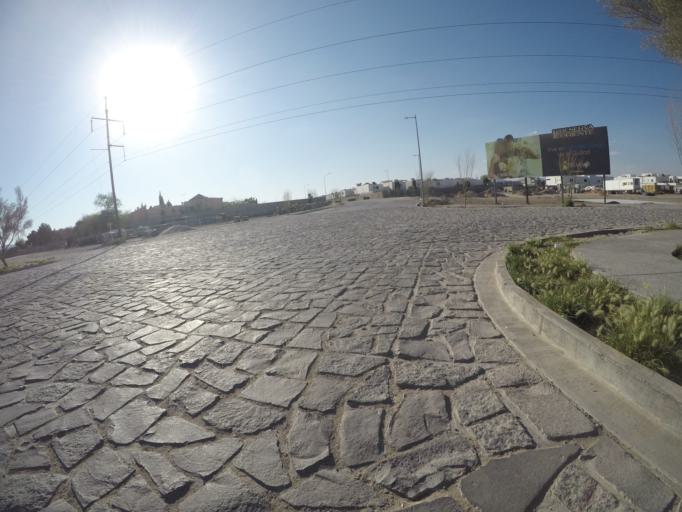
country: MX
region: Chihuahua
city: Ciudad Juarez
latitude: 31.7025
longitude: -106.3919
